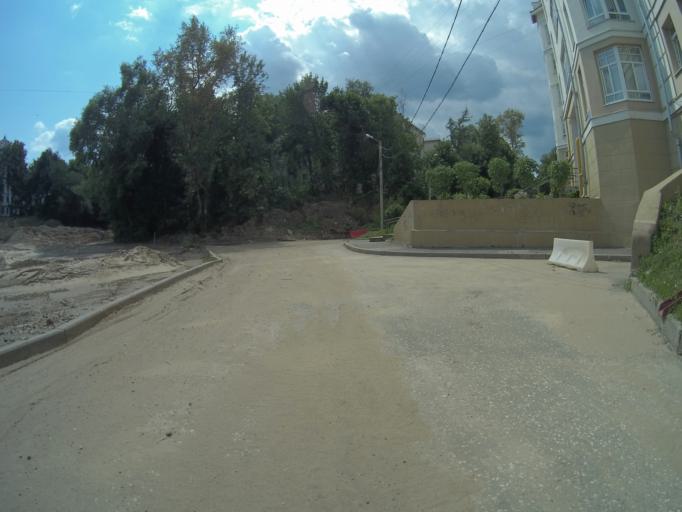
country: RU
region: Vladimir
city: Vladimir
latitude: 56.1322
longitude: 40.3913
